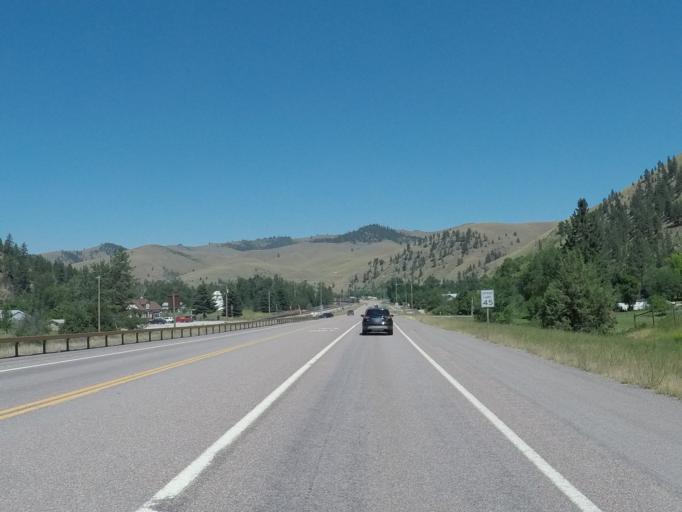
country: US
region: Montana
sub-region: Missoula County
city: Frenchtown
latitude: 47.2681
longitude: -114.1758
